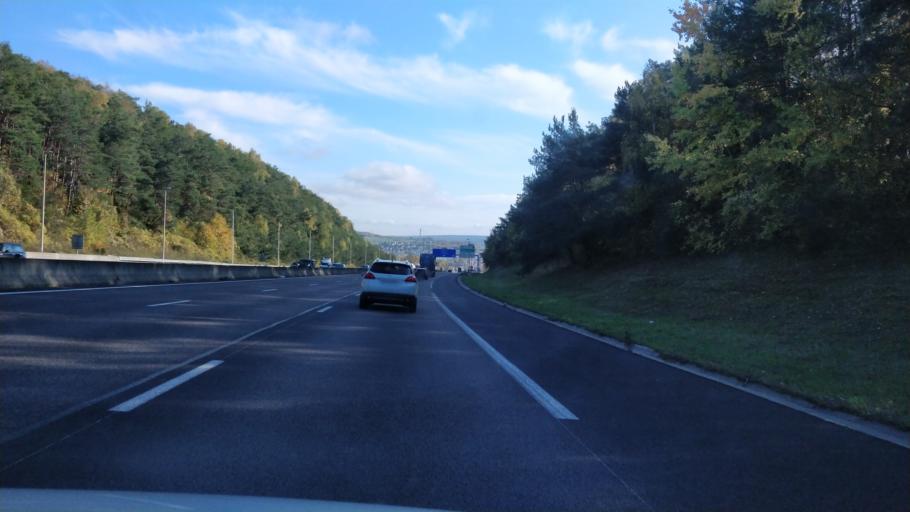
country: FR
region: Haute-Normandie
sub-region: Departement de la Seine-Maritime
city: Oissel
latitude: 49.3414
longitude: 1.0657
